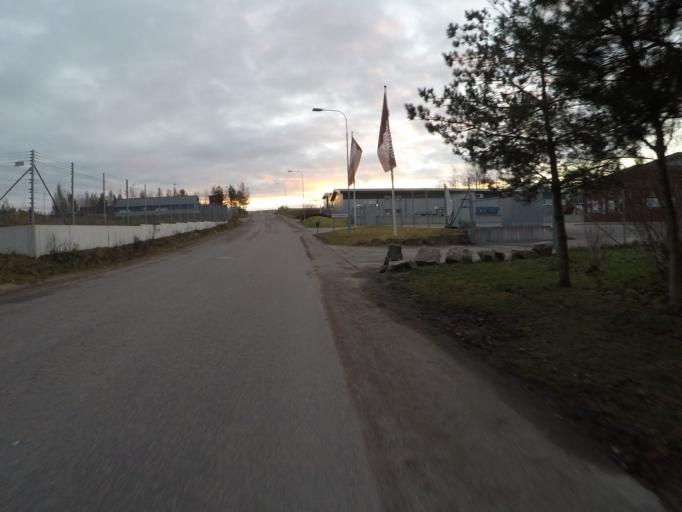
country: SE
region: Skane
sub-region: Sjobo Kommun
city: Sjoebo
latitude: 55.6391
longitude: 13.6859
